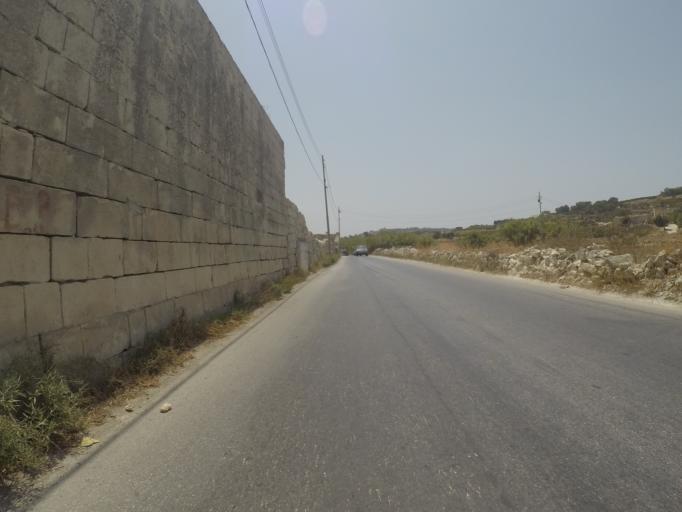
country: MT
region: Ir-Rabat
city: Rabat
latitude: 35.8705
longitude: 14.4142
